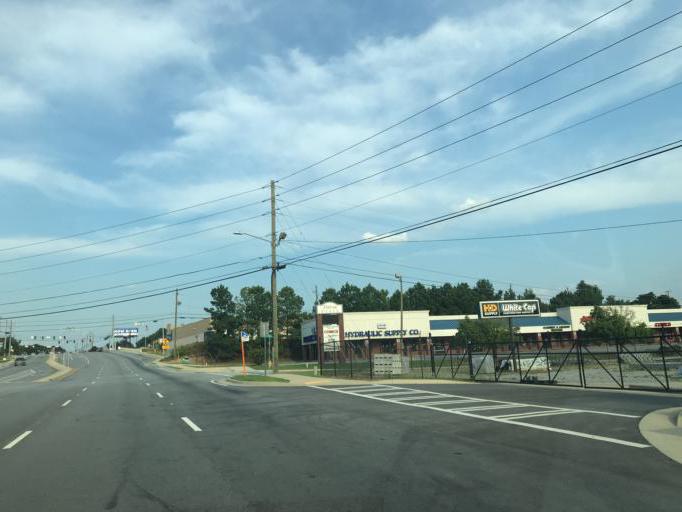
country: US
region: Alabama
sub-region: Russell County
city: Phenix City
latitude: 32.5395
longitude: -84.9579
